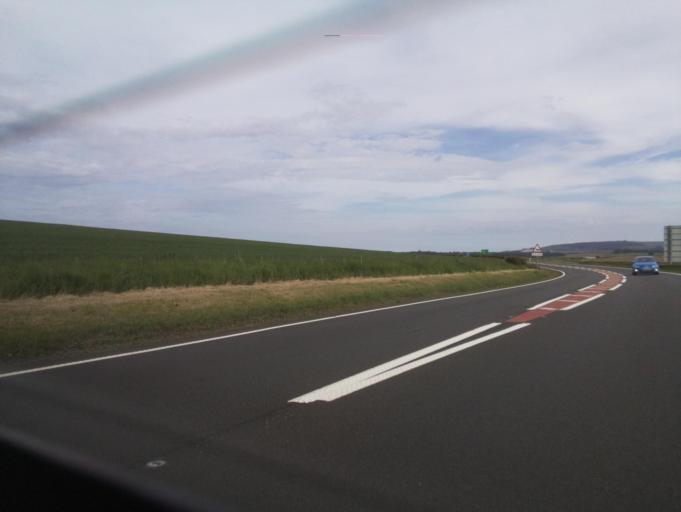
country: GB
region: Scotland
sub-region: The Scottish Borders
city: Chirnside
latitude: 55.8540
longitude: -2.1800
